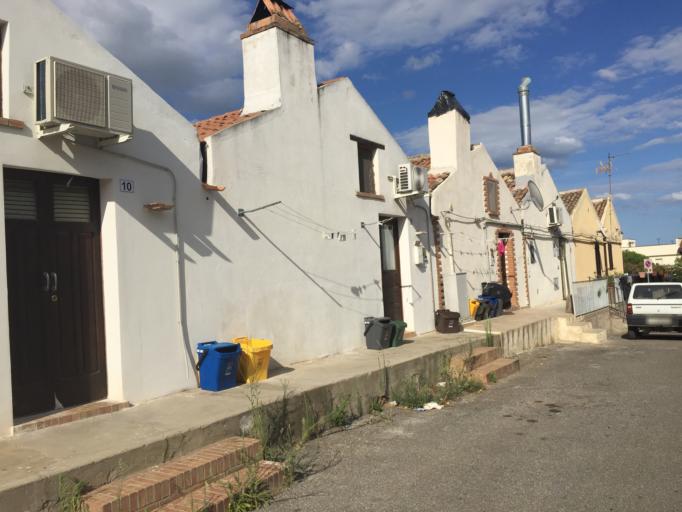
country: IT
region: Basilicate
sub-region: Provincia di Matera
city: Policoro
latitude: 40.2153
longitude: 16.6802
